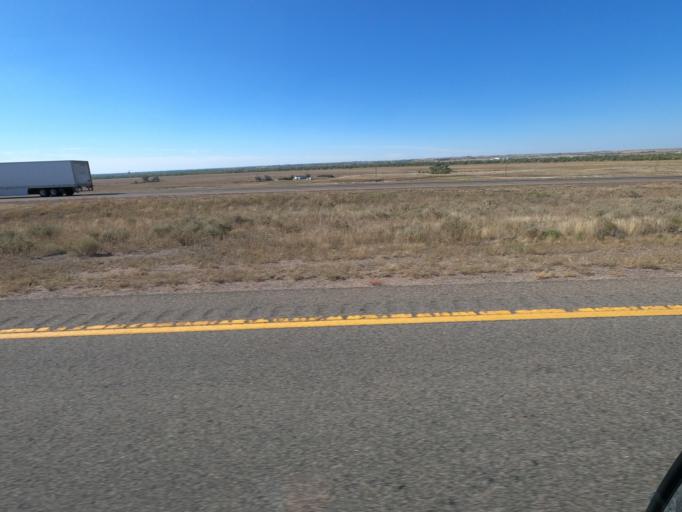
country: US
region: Colorado
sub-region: Logan County
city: Sterling
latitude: 40.6441
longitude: -103.1506
